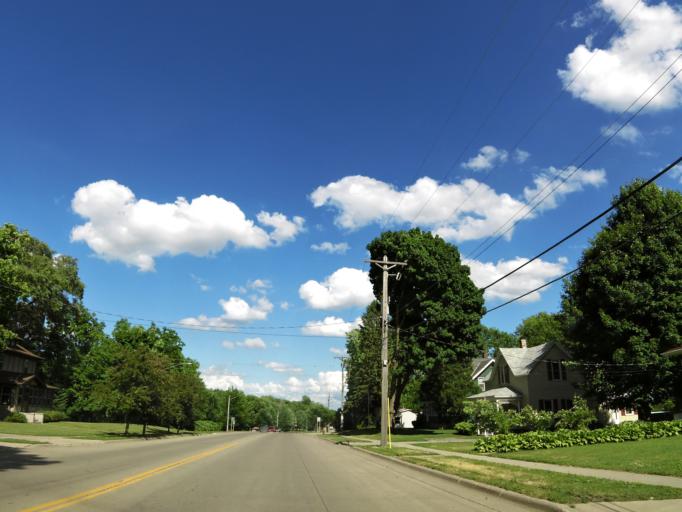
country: US
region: Minnesota
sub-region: Meeker County
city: Dassel
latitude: 45.0814
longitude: -94.3039
